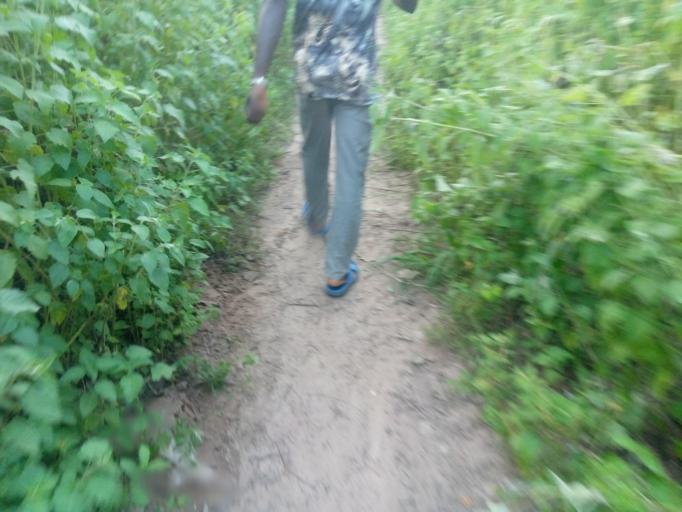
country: GM
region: Western
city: Gunjur
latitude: 13.0422
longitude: -16.7281
